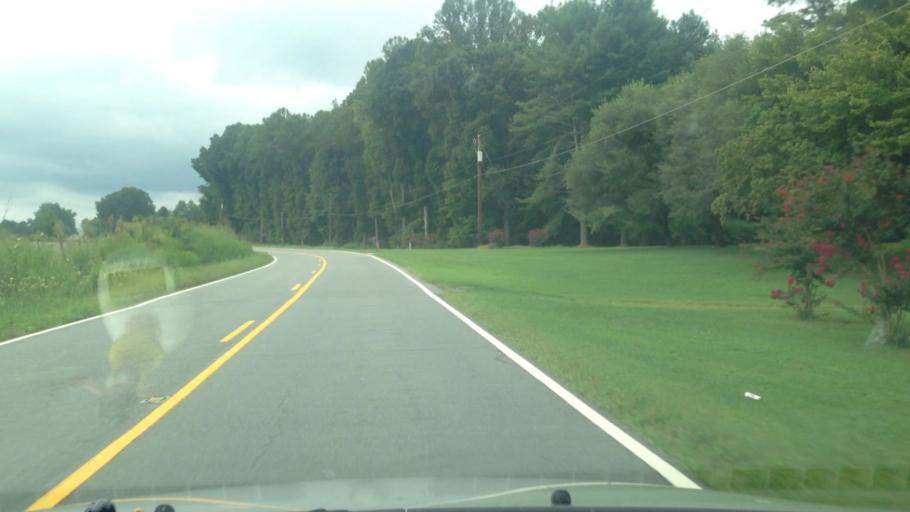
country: US
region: North Carolina
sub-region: Stokes County
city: Walnut Cove
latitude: 36.2475
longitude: -80.1526
